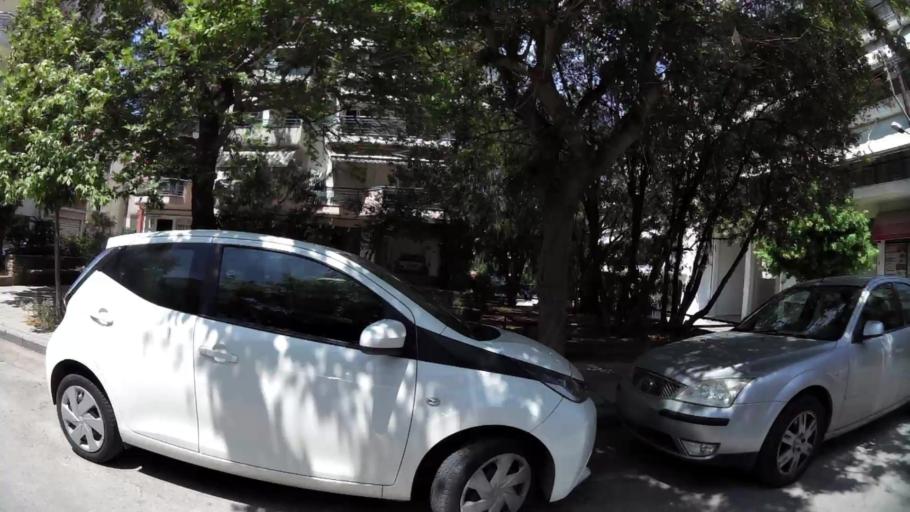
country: GR
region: Central Macedonia
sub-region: Nomos Thessalonikis
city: Triandria
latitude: 40.6188
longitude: 22.9738
